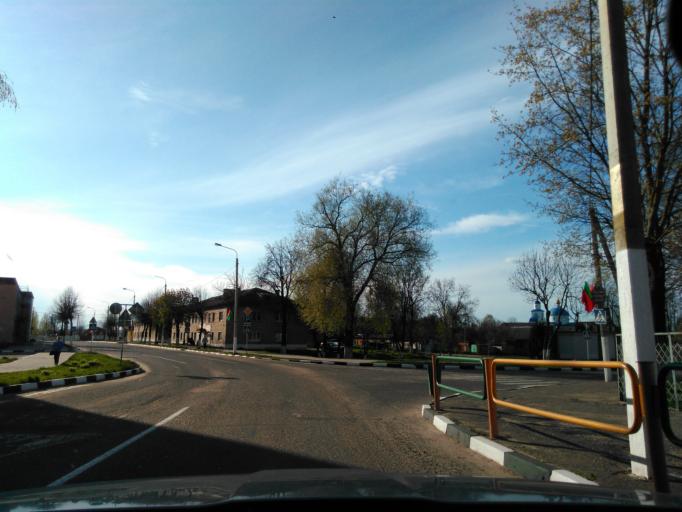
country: BY
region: Vitebsk
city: Chashniki
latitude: 54.8596
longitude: 29.1638
